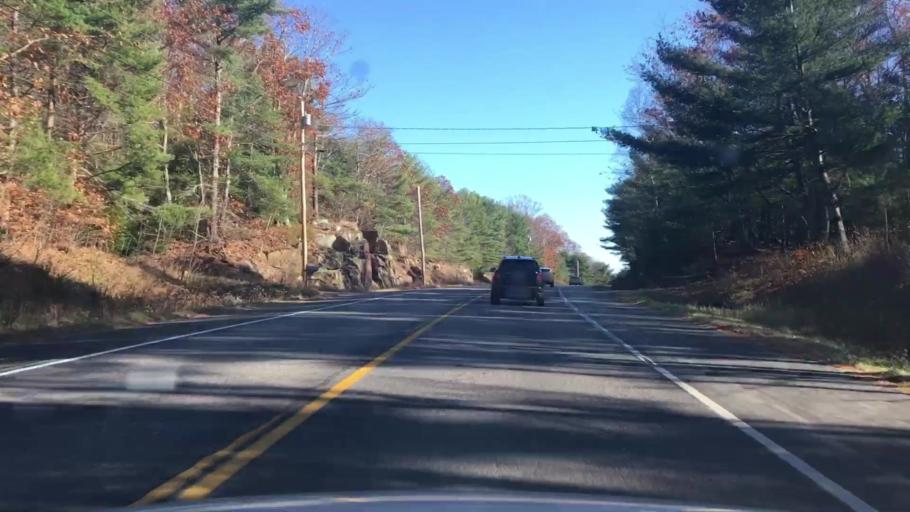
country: US
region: Maine
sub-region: Knox County
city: Union
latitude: 44.2144
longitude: -69.2330
